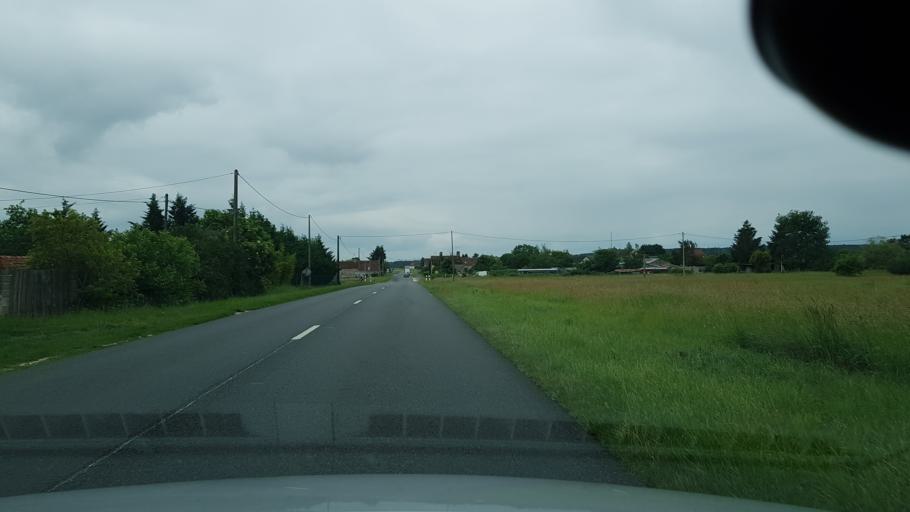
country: FR
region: Centre
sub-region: Departement du Loir-et-Cher
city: Chatillon-sur-Cher
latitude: 47.3086
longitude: 1.5054
